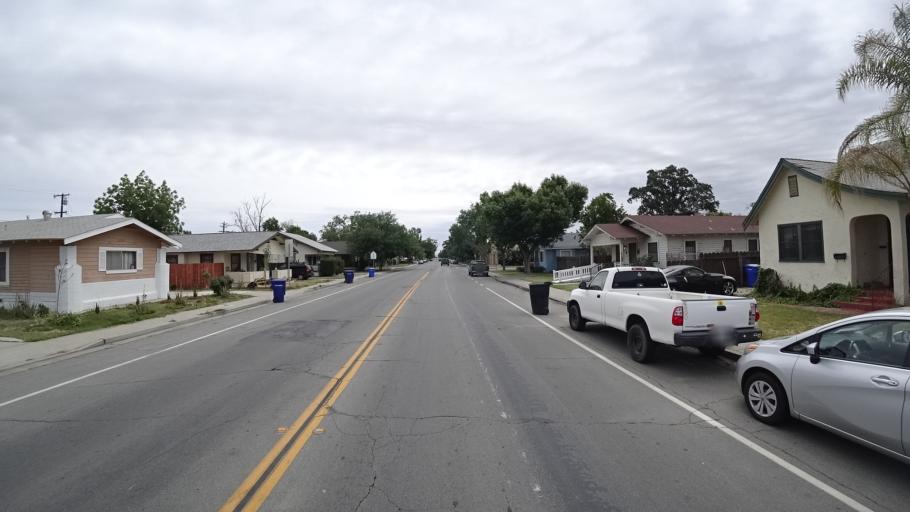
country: US
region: California
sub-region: Kings County
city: Hanford
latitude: 36.3349
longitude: -119.6516
